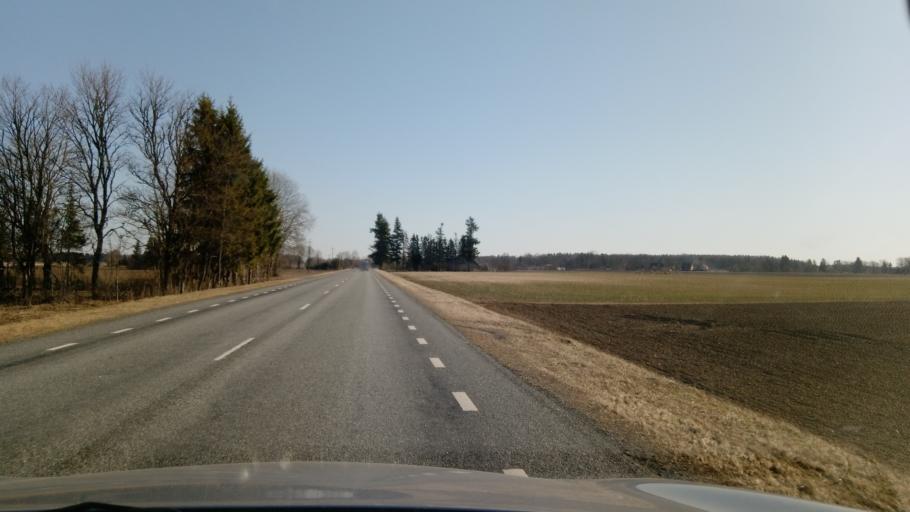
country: EE
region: Jaervamaa
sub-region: Jaerva-Jaani vald
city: Jarva-Jaani
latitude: 59.0741
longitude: 25.9522
